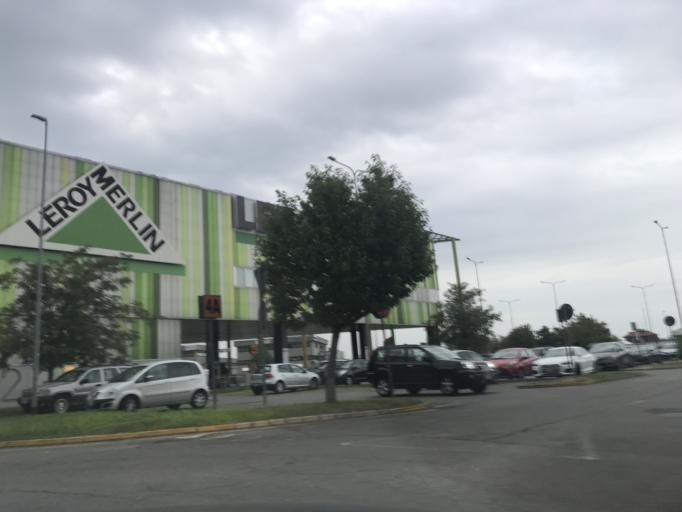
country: IT
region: Lombardy
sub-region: Citta metropolitana di Milano
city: Rozzano
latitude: 45.4055
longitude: 9.1539
